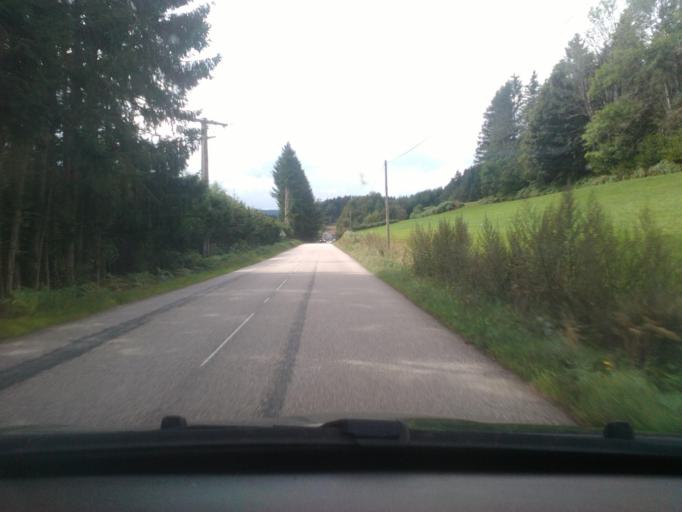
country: FR
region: Lorraine
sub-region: Departement des Vosges
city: Corcieux
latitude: 48.1463
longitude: 6.8579
